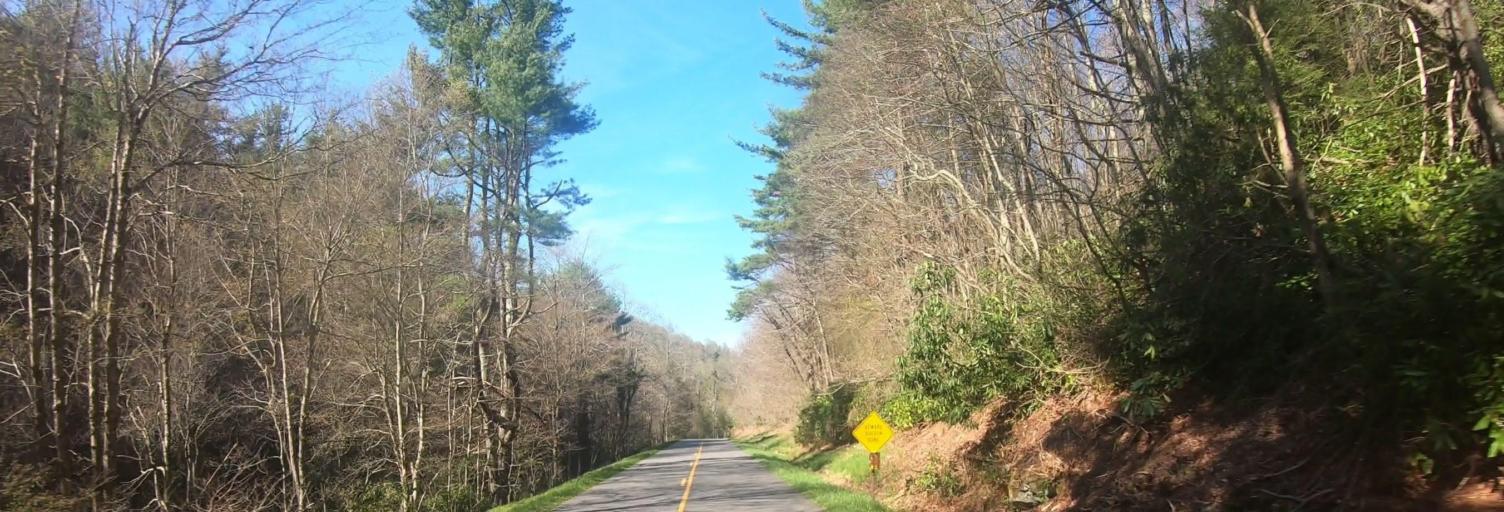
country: US
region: North Carolina
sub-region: Watauga County
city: Blowing Rock
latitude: 36.1709
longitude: -81.6151
